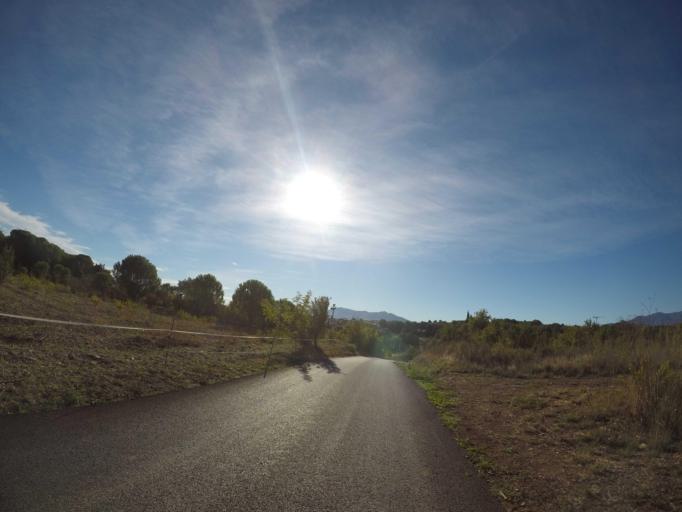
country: FR
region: Languedoc-Roussillon
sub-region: Departement des Pyrenees-Orientales
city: Llupia
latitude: 42.5839
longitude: 2.7724
